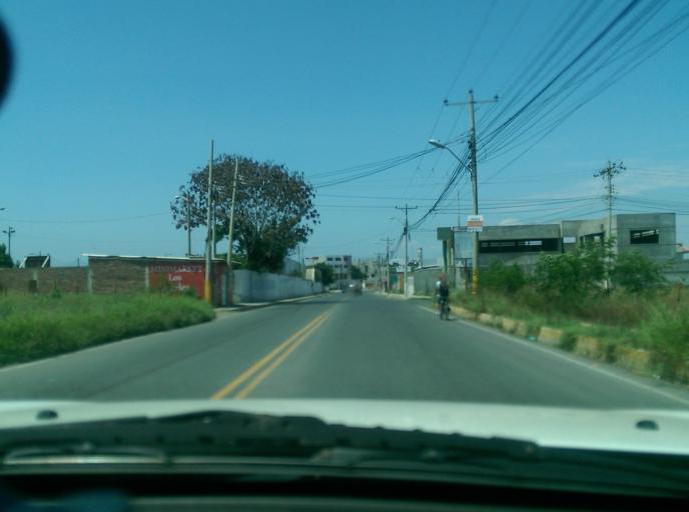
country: EC
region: Manabi
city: Manta
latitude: -0.9580
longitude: -80.7572
